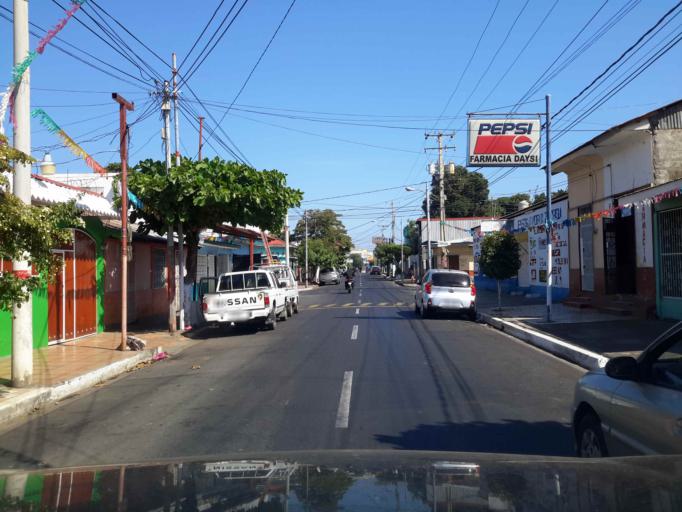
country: NI
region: Managua
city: Managua
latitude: 12.1491
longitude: -86.2945
